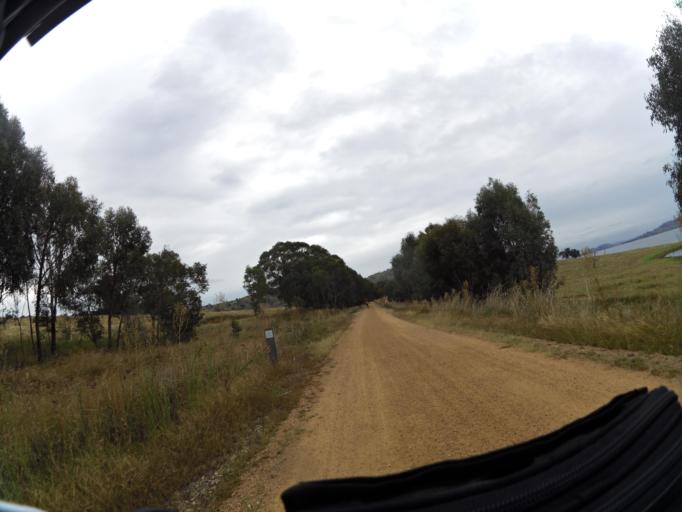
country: AU
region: New South Wales
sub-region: Albury Municipality
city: East Albury
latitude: -36.1997
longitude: 147.0437
